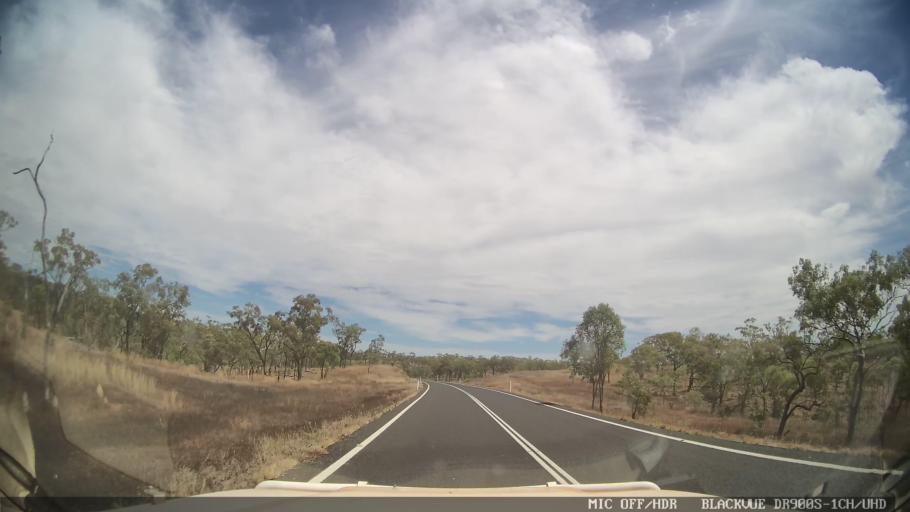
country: AU
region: Queensland
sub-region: Cairns
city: Port Douglas
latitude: -16.1415
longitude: 144.7707
